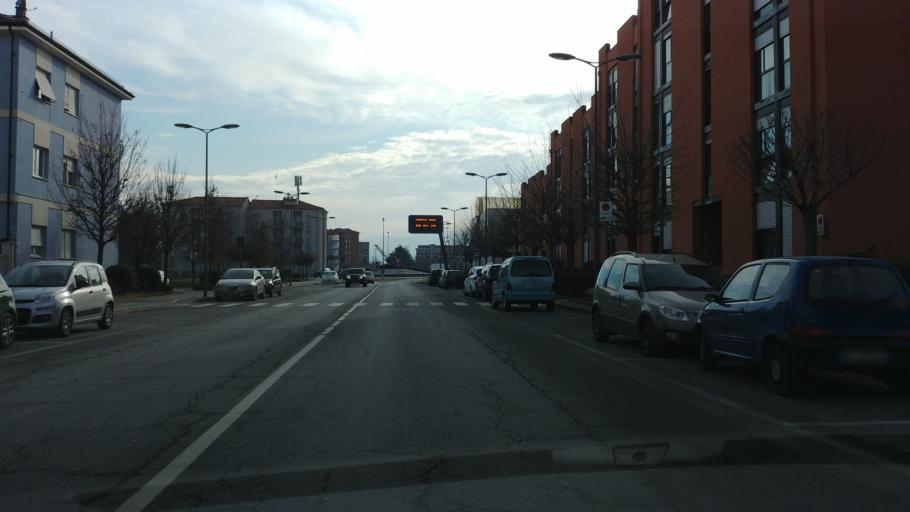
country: IT
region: Piedmont
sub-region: Provincia di Cuneo
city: Cuneo
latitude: 44.3779
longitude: 7.5335
